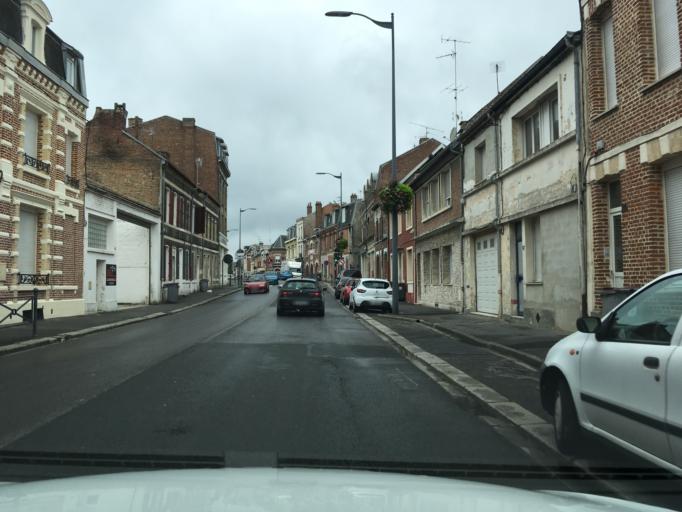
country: FR
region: Picardie
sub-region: Departement de l'Aisne
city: Harly
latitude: 49.8402
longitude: 3.3043
